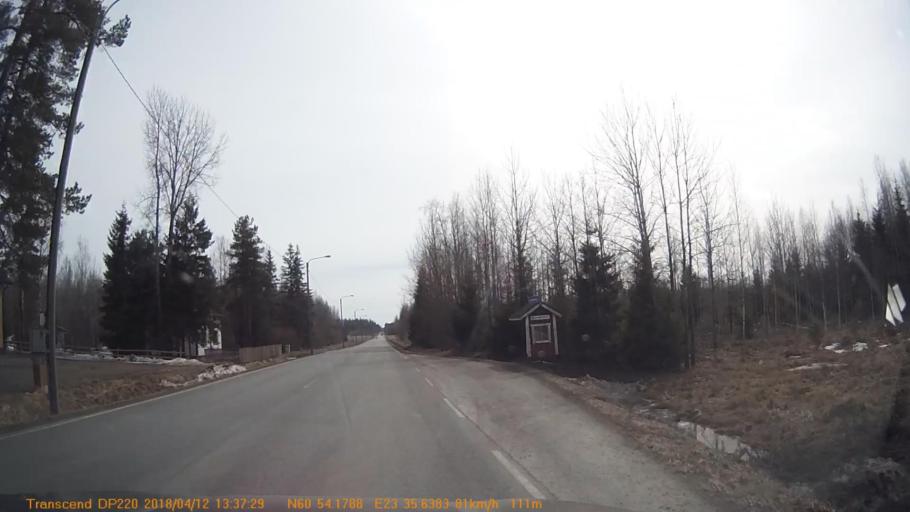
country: FI
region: Haeme
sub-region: Forssa
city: Forssa
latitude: 60.9026
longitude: 23.5941
